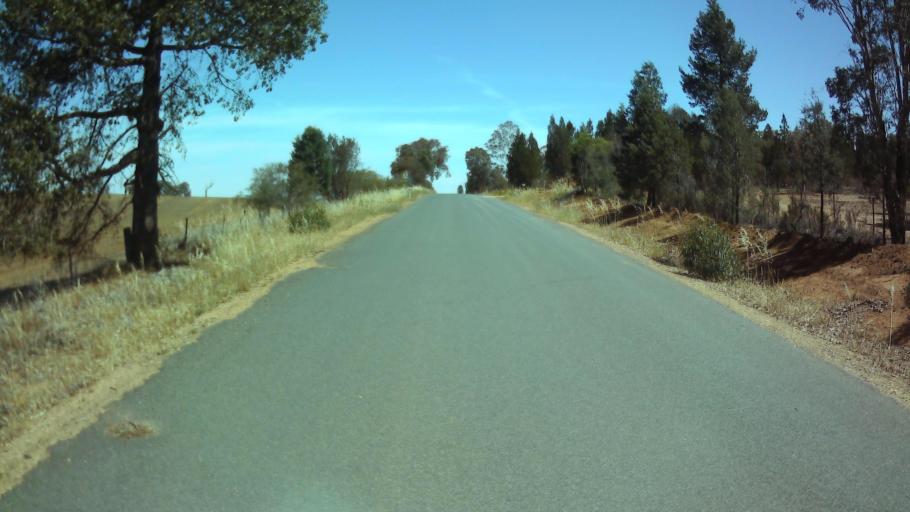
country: AU
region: New South Wales
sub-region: Weddin
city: Grenfell
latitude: -33.9028
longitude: 148.1835
